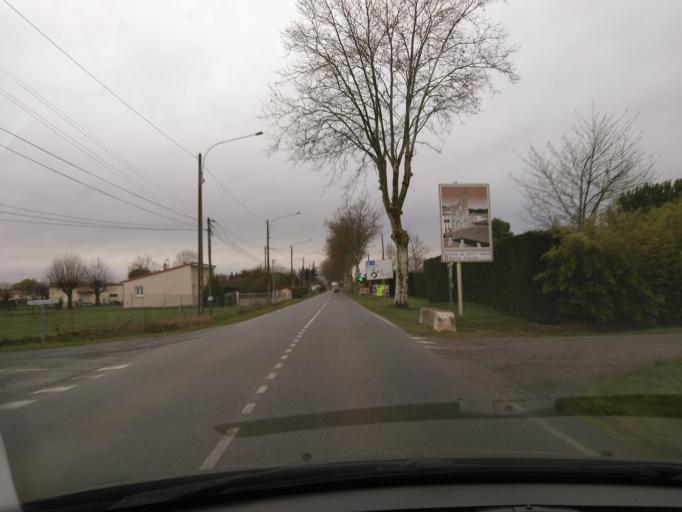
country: FR
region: Midi-Pyrenees
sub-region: Departement de la Haute-Garonne
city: Montesquieu-Volvestre
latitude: 43.1955
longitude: 1.2332
